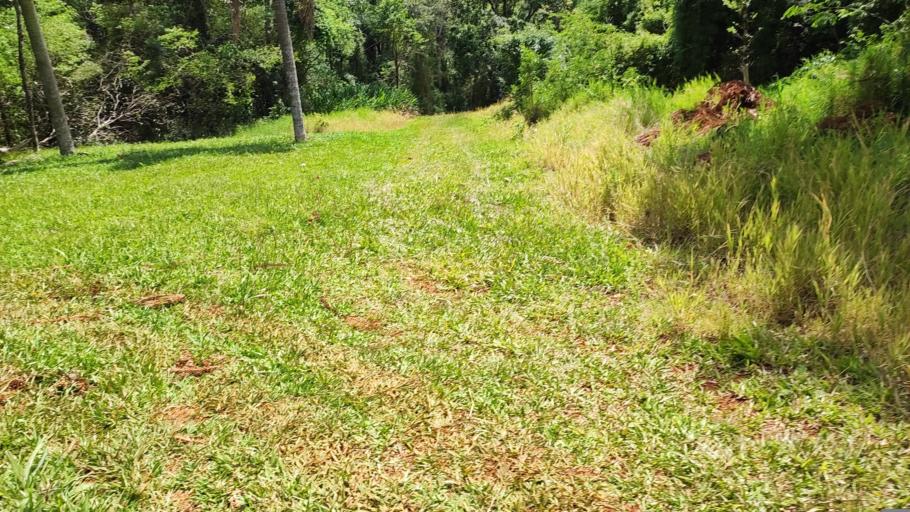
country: AR
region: Misiones
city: Dos de Mayo
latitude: -26.9992
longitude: -54.6263
